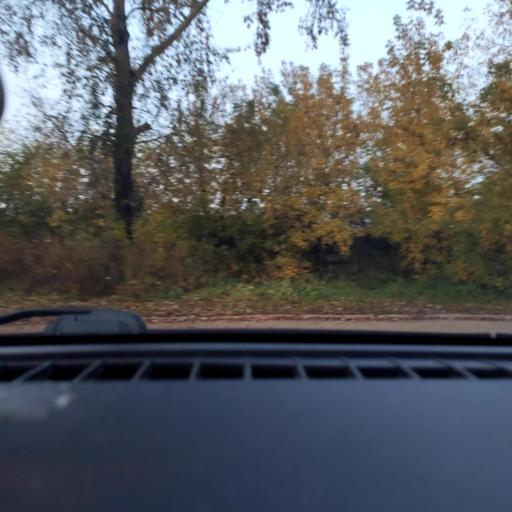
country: RU
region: Perm
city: Perm
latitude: 57.9737
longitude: 56.2134
